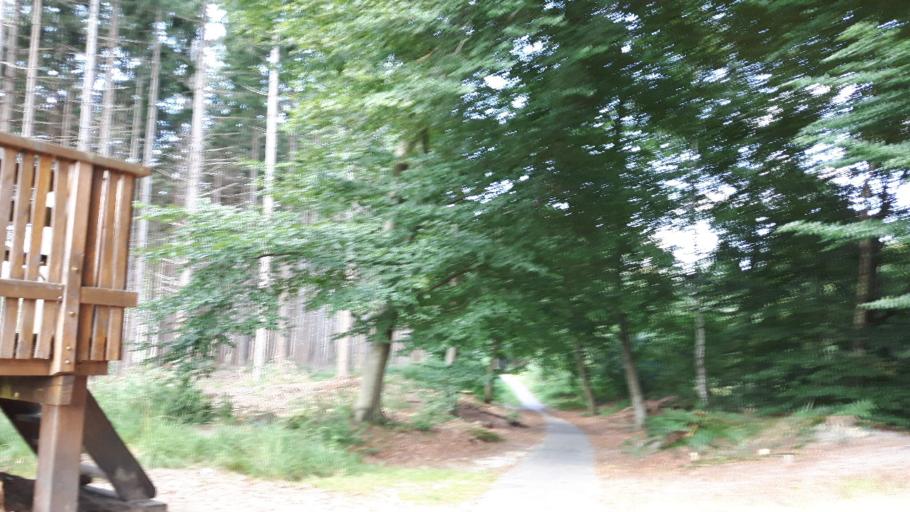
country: NL
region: Friesland
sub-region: Gemeente Smallingerland
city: Drachtstercompagnie
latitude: 53.0777
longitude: 6.2428
